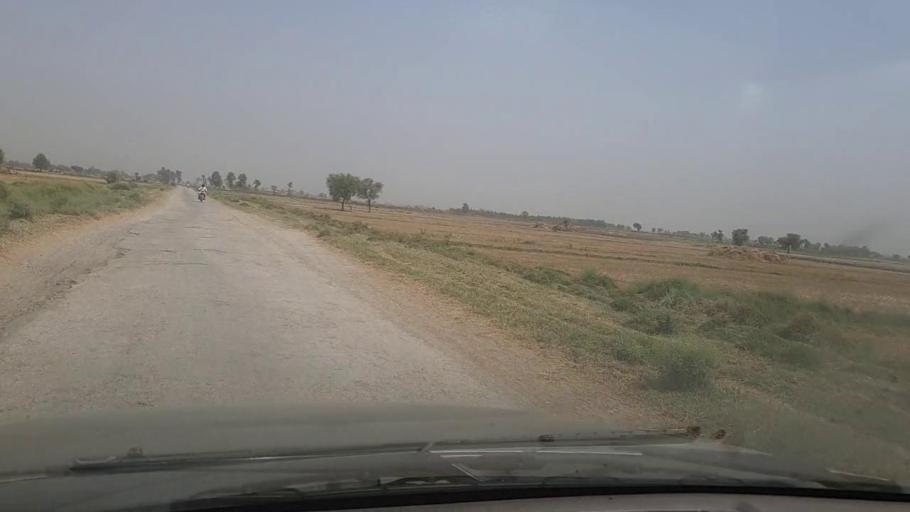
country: PK
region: Sindh
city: Madeji
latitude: 27.8132
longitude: 68.3979
